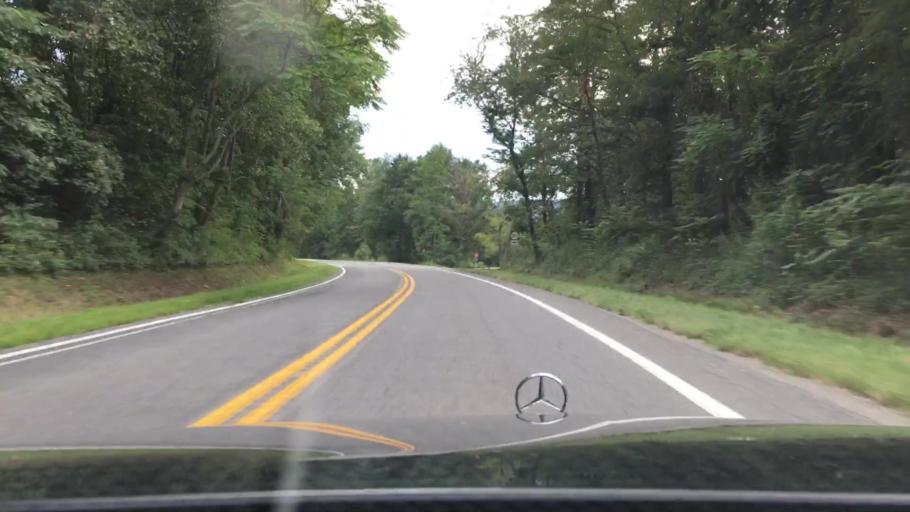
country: US
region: Virginia
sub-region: City of Waynesboro
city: Waynesboro
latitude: 38.0259
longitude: -78.8127
